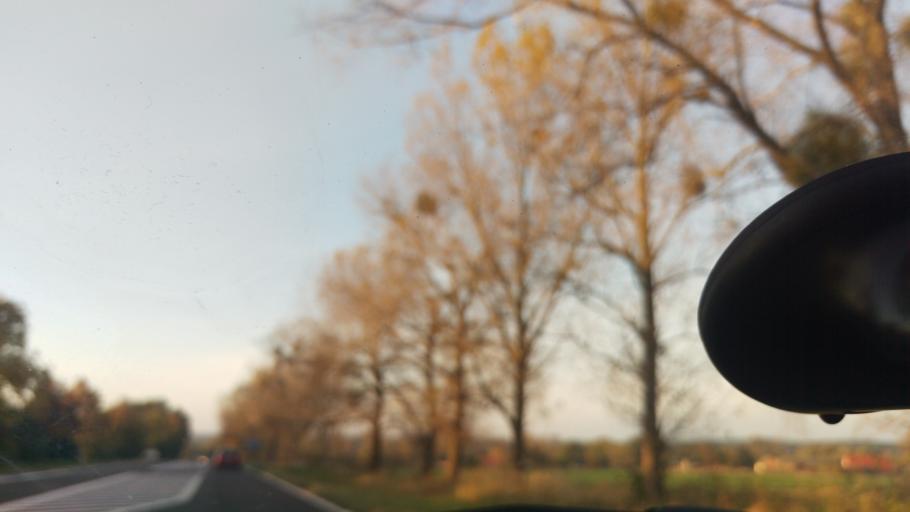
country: PL
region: West Pomeranian Voivodeship
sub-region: Powiat gryfinski
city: Stare Czarnowo
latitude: 53.2344
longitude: 14.7890
